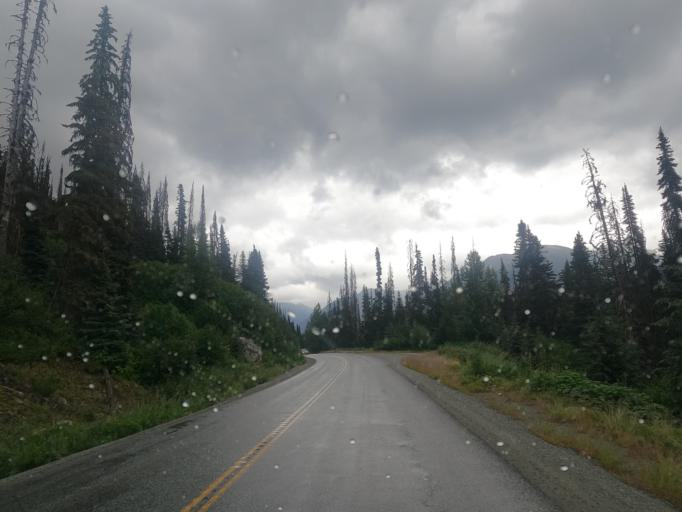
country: CA
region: British Columbia
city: Pemberton
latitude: 50.3859
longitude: -122.4474
